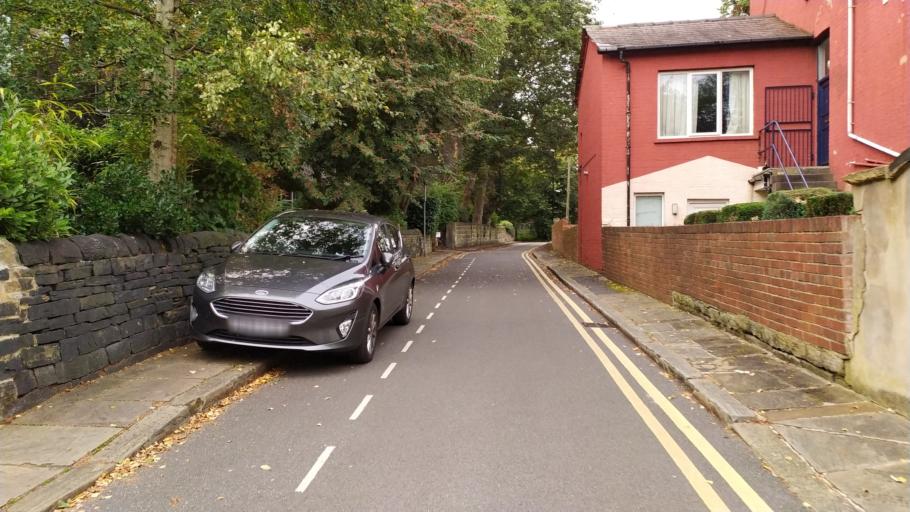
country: GB
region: England
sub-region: City and Borough of Leeds
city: Leeds
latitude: 53.8173
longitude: -1.5614
